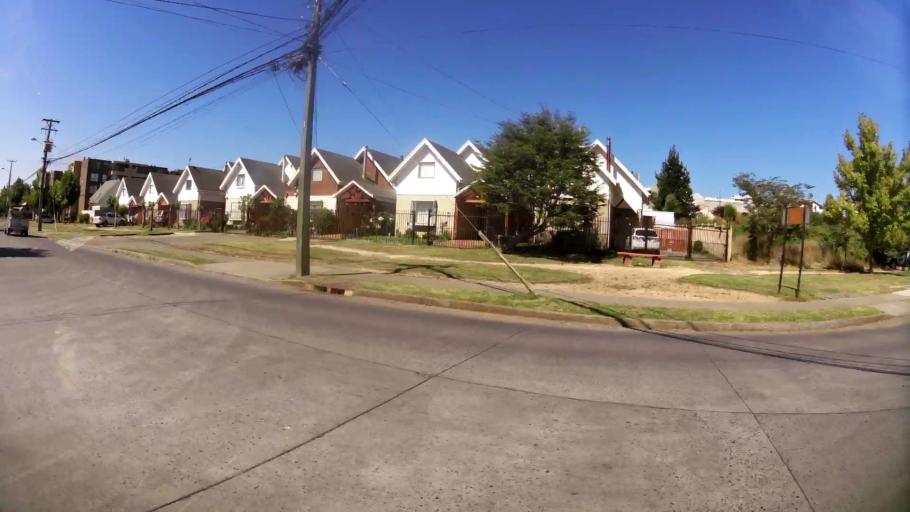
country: CL
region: Biobio
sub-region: Provincia de Concepcion
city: Concepcion
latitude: -36.7819
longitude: -73.0451
